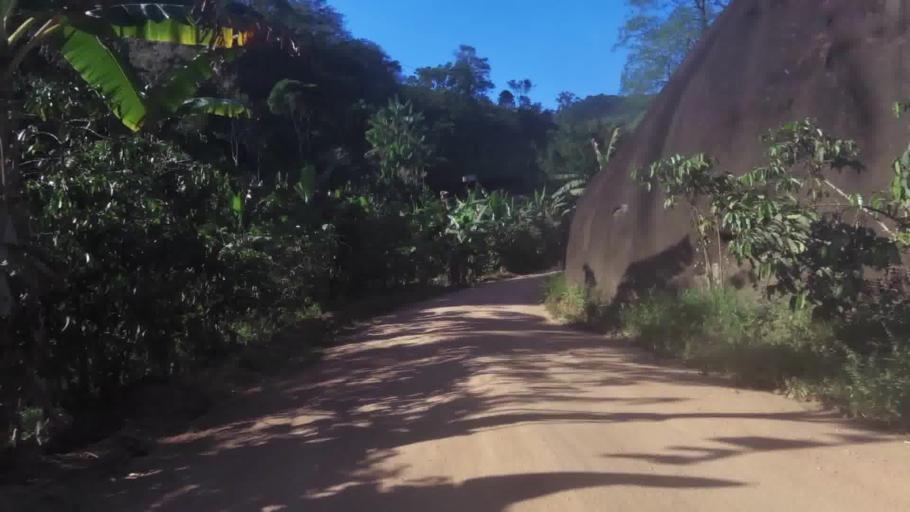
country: BR
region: Espirito Santo
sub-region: Iconha
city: Iconha
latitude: -20.7584
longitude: -40.8185
